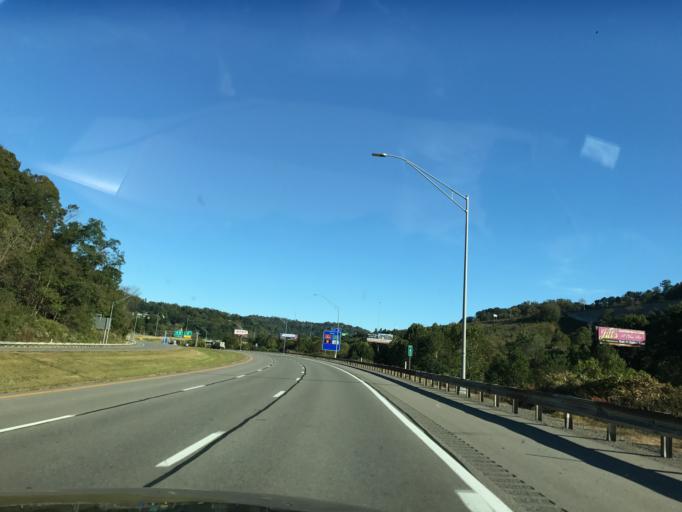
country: US
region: West Virginia
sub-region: Ohio County
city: Bethlehem
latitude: 40.0535
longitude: -80.6762
